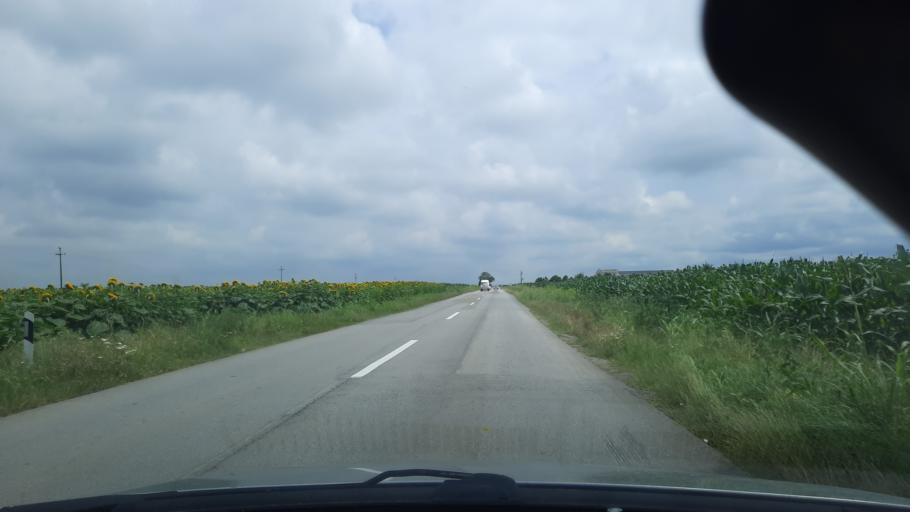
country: RS
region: Central Serbia
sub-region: Branicevski Okrug
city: Malo Crnice
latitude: 44.5858
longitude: 21.2879
